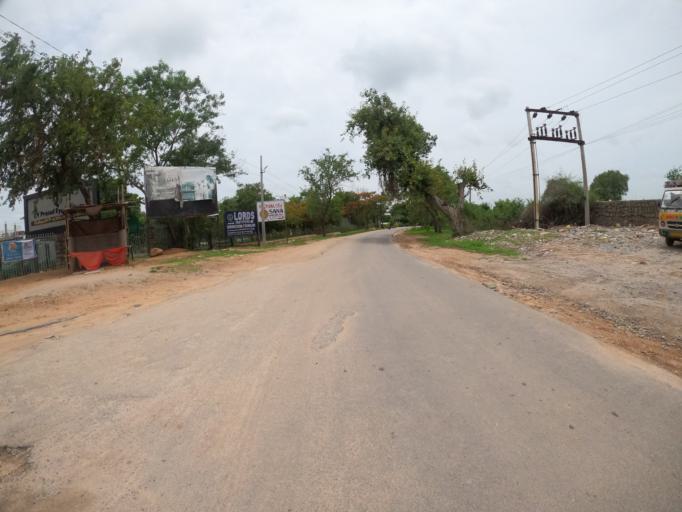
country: IN
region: Telangana
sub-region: Hyderabad
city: Hyderabad
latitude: 17.3413
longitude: 78.3727
